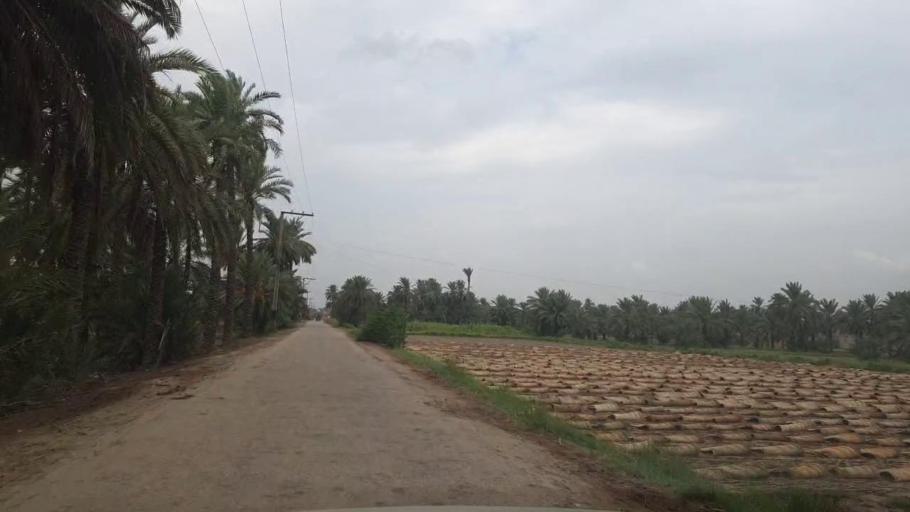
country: PK
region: Sindh
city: Khairpur
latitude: 27.5414
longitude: 68.7458
